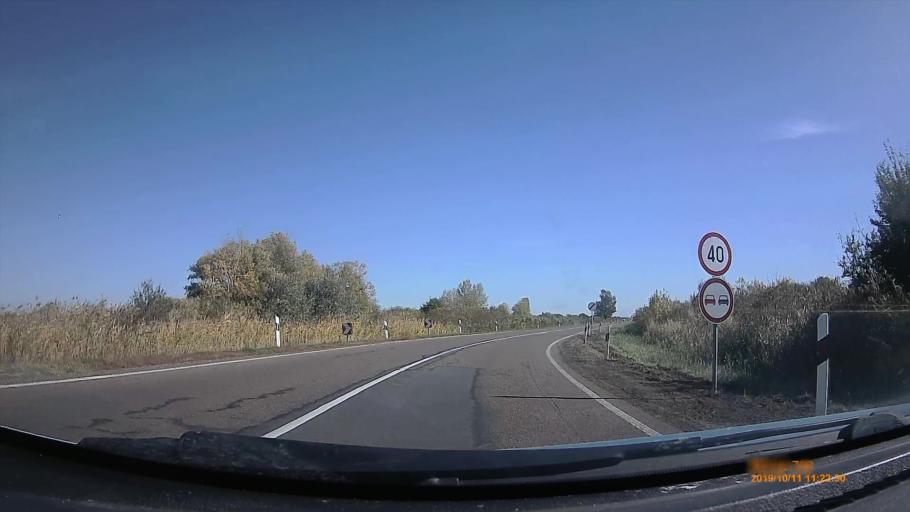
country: HU
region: Hajdu-Bihar
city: Tiszacsege
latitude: 47.5873
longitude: 21.0107
